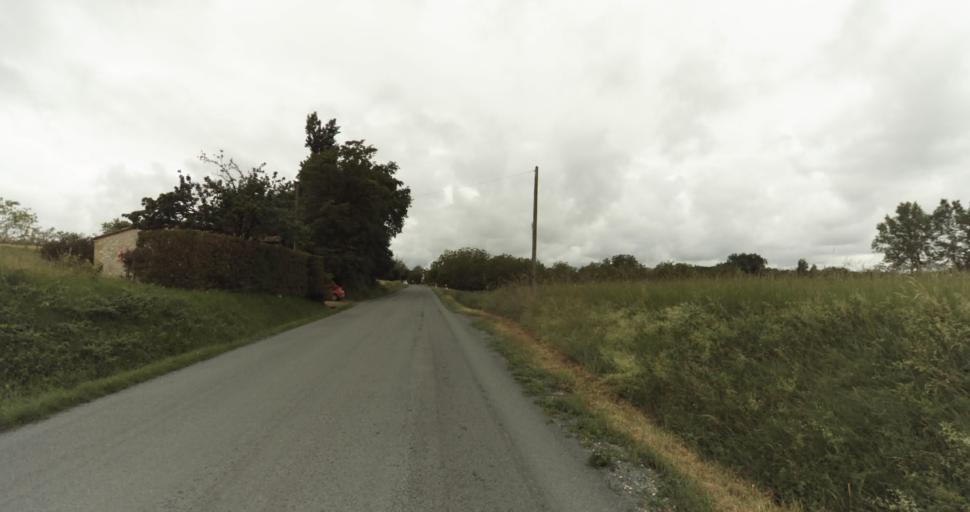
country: FR
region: Aquitaine
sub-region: Departement de la Dordogne
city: Beaumont-du-Perigord
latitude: 44.7051
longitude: 0.8329
